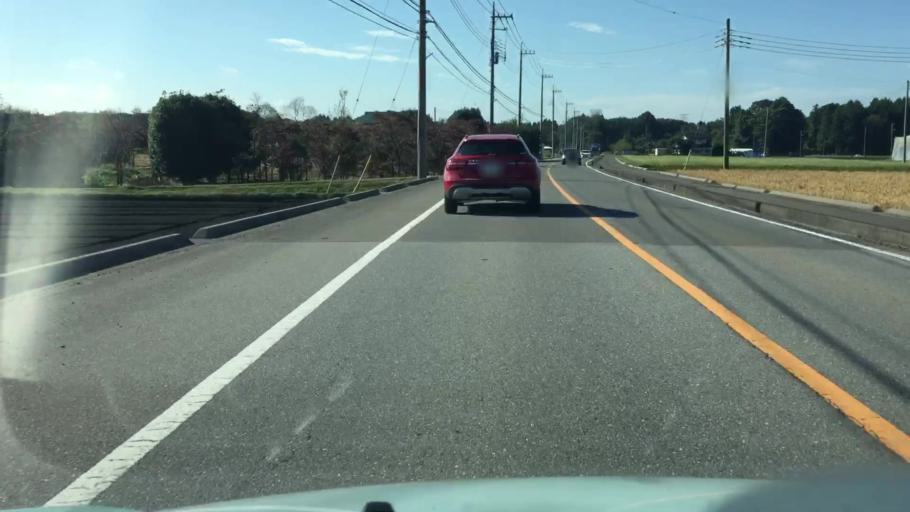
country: JP
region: Tochigi
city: Utsunomiya-shi
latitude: 36.5807
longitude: 139.9815
